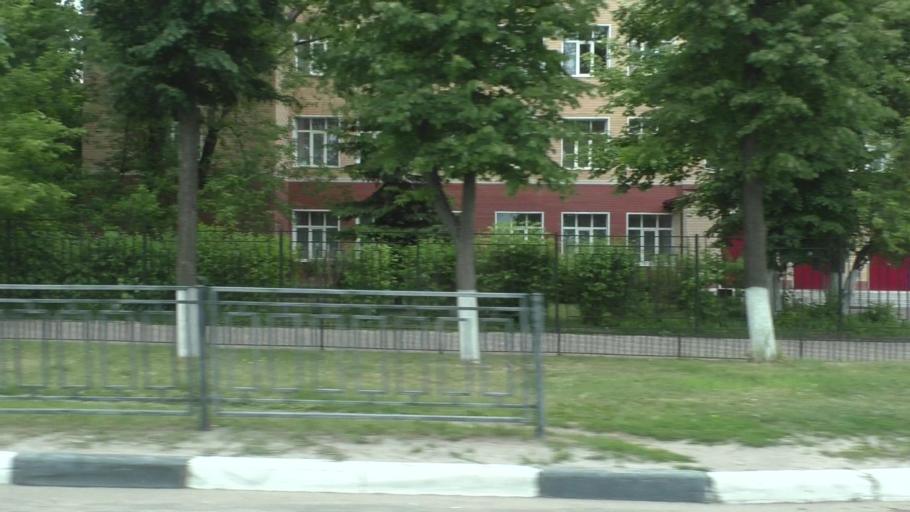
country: RU
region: Moskovskaya
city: Yegor'yevsk
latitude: 55.3743
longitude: 39.0495
